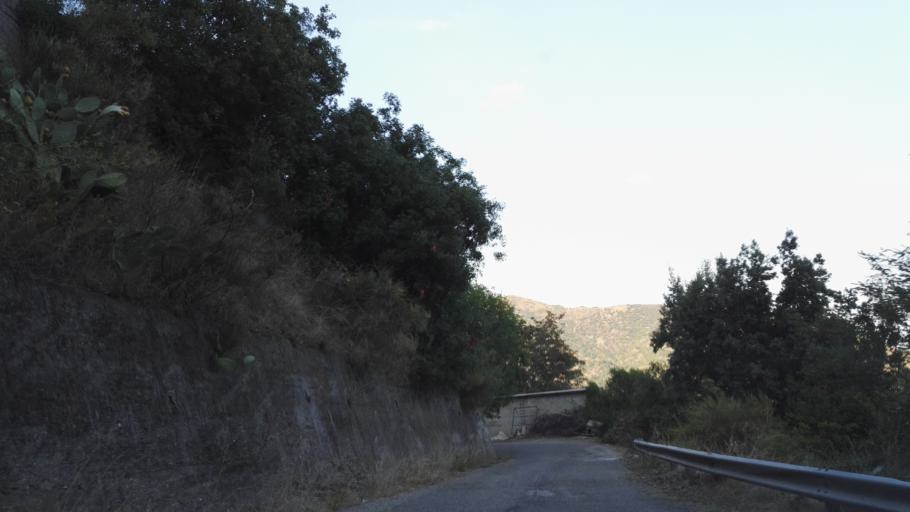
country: IT
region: Calabria
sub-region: Provincia di Reggio Calabria
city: Caulonia
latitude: 38.4106
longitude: 16.3674
